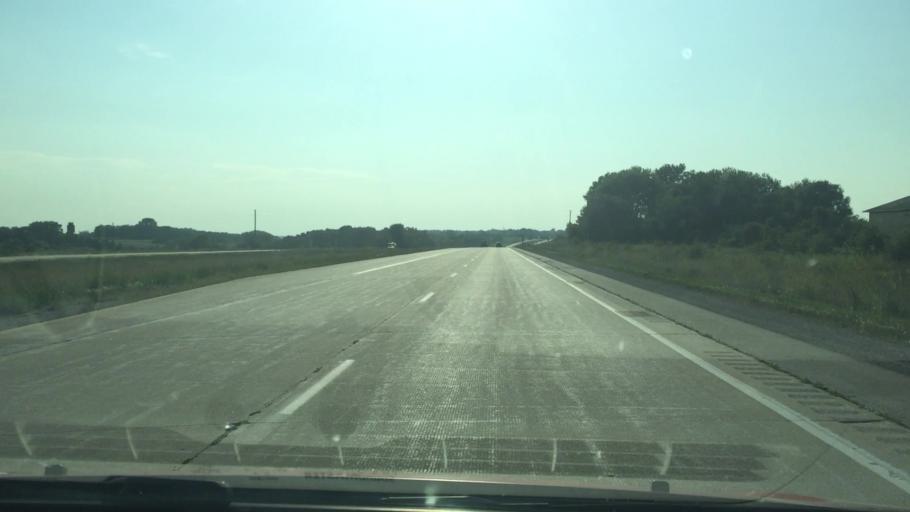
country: US
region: Iowa
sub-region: Scott County
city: Blue Grass
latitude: 41.5129
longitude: -90.7909
